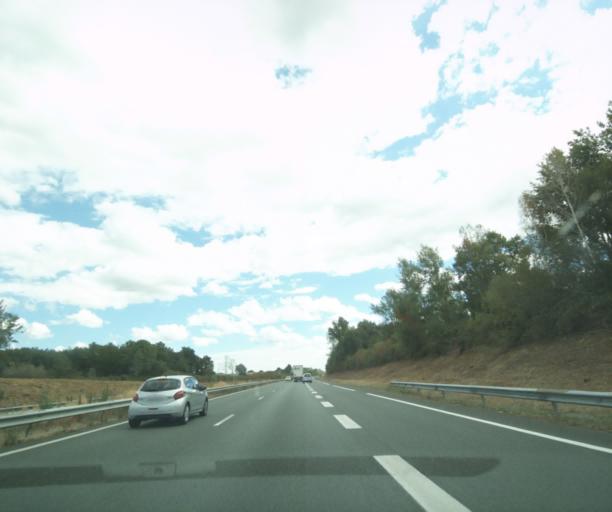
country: FR
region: Aquitaine
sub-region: Departement de la Gironde
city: La Reole
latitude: 44.5073
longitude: -0.0458
